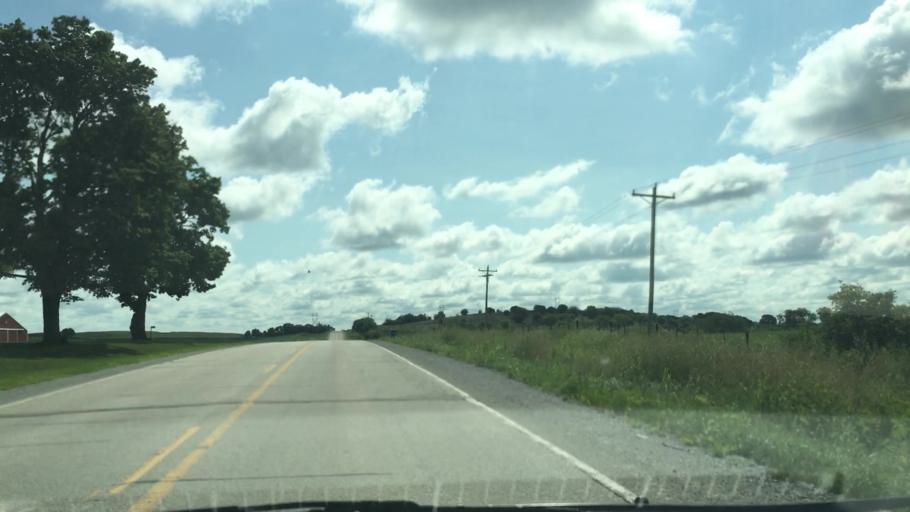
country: US
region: Iowa
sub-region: Johnson County
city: Solon
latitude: 41.8313
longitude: -91.4937
